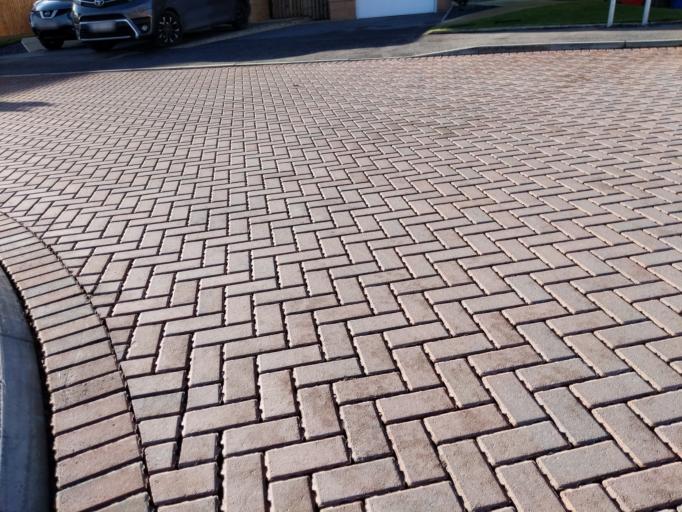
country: GB
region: Scotland
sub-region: Midlothian
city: Loanhead
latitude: 55.8520
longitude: -3.1433
